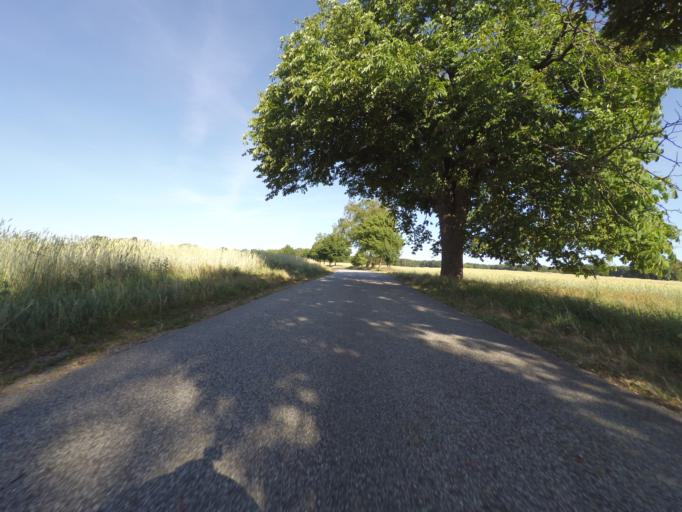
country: DE
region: Mecklenburg-Vorpommern
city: Lubz
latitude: 53.3805
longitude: 12.0390
